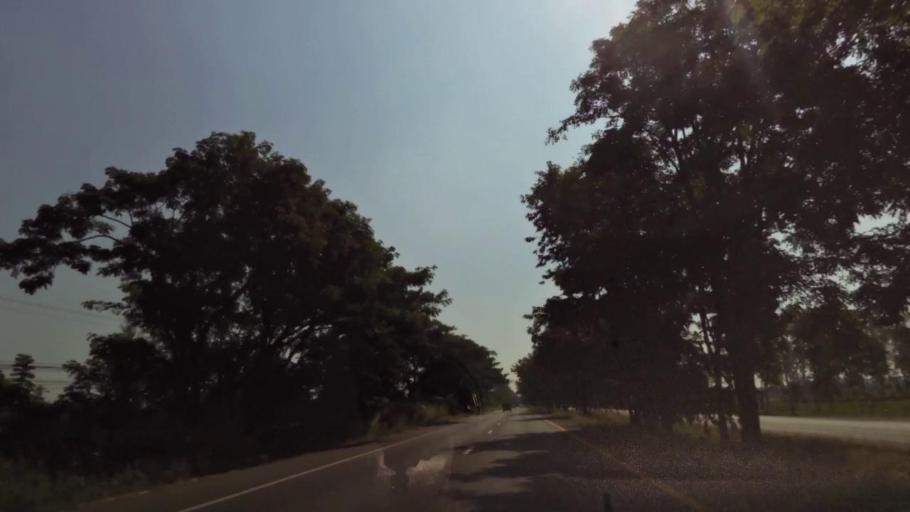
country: TH
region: Nakhon Sawan
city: Kao Liao
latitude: 15.9722
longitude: 100.1192
